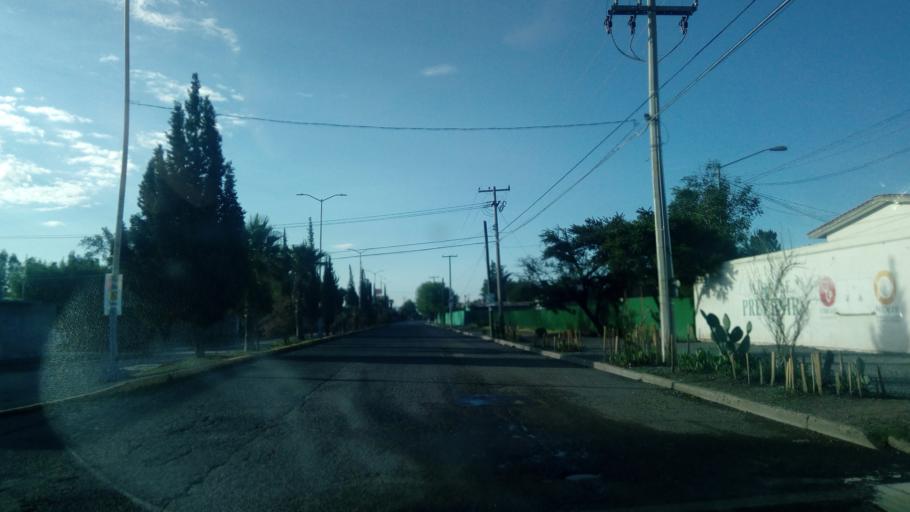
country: MX
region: Durango
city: Victoria de Durango
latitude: 24.0541
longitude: -104.6086
